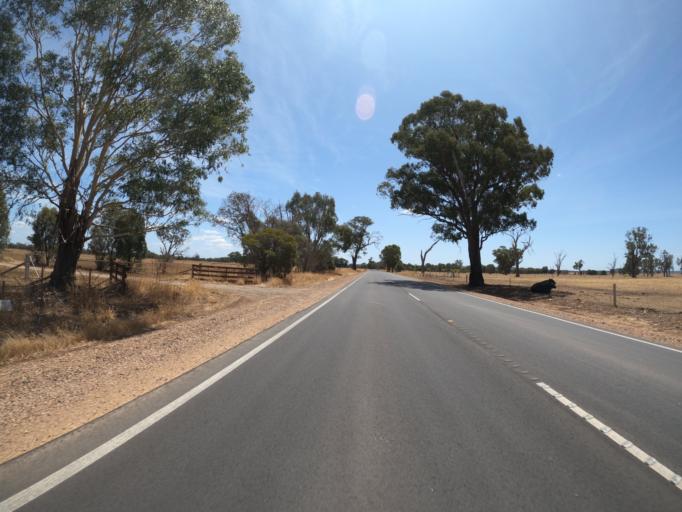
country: AU
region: Victoria
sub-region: Benalla
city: Benalla
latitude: -36.5015
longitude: 146.0226
